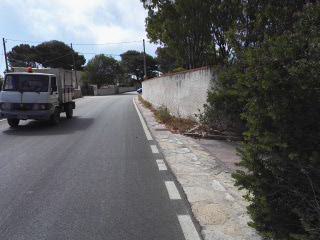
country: IT
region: Sicily
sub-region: Trapani
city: Favignana
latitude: 37.9210
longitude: 12.3441
